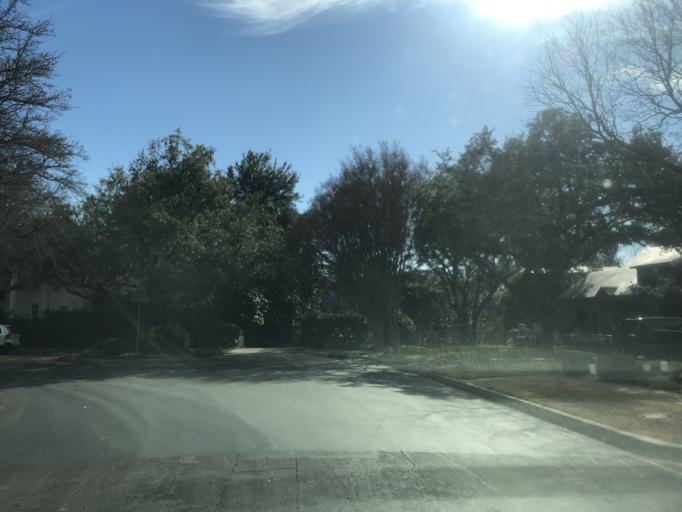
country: US
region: Texas
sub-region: Dallas County
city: Highland Park
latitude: 32.8215
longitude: -96.7969
